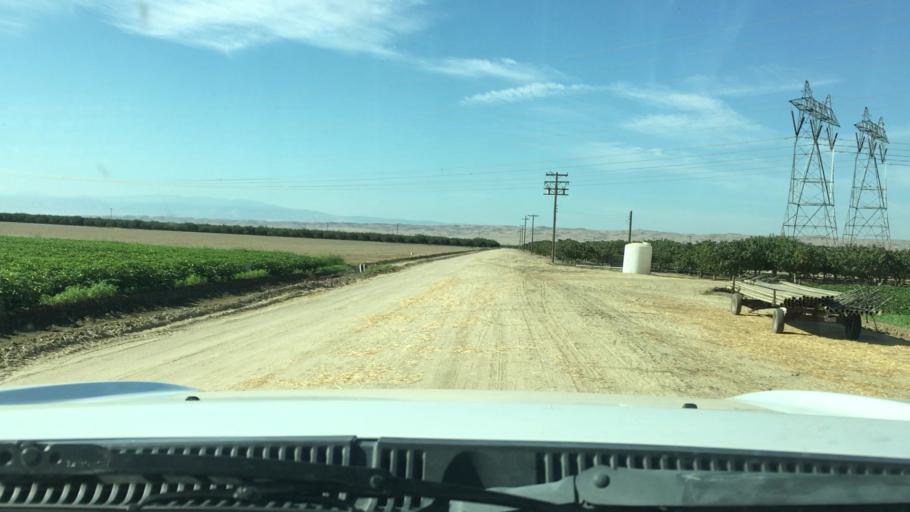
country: US
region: California
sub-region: Kern County
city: Buttonwillow
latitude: 35.3808
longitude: -119.4035
